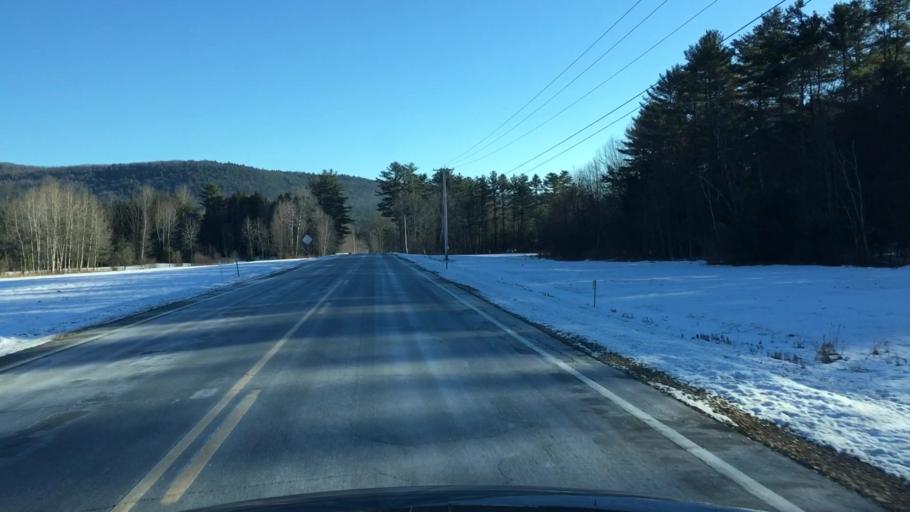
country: US
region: New Hampshire
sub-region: Grafton County
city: Woodsville
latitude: 44.2531
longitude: -72.0497
